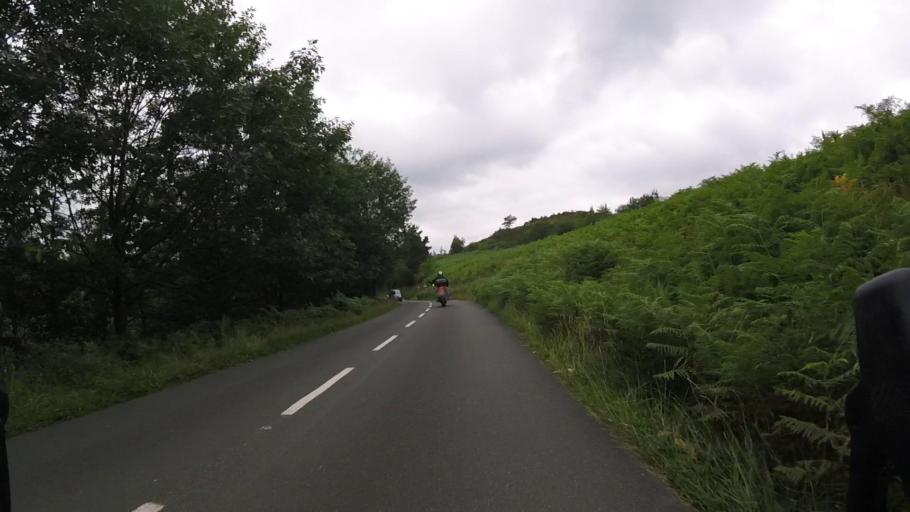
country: ES
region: Basque Country
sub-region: Provincia de Guipuzcoa
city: Irun
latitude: 43.2732
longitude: -1.8082
